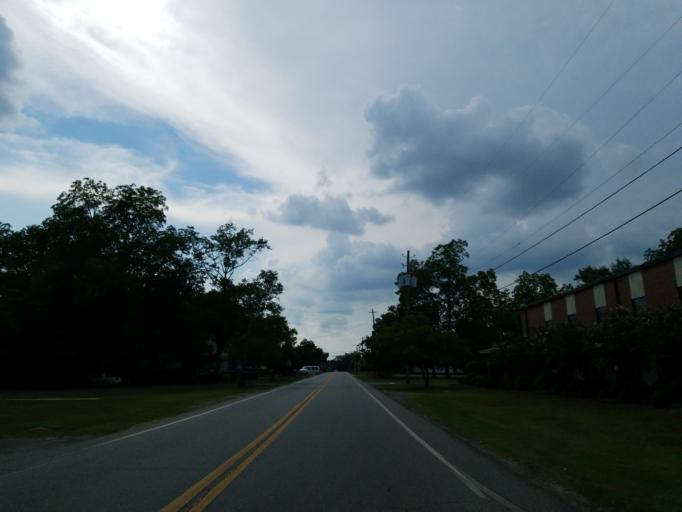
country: US
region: Georgia
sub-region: Dooly County
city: Unadilla
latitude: 32.2606
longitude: -83.7327
